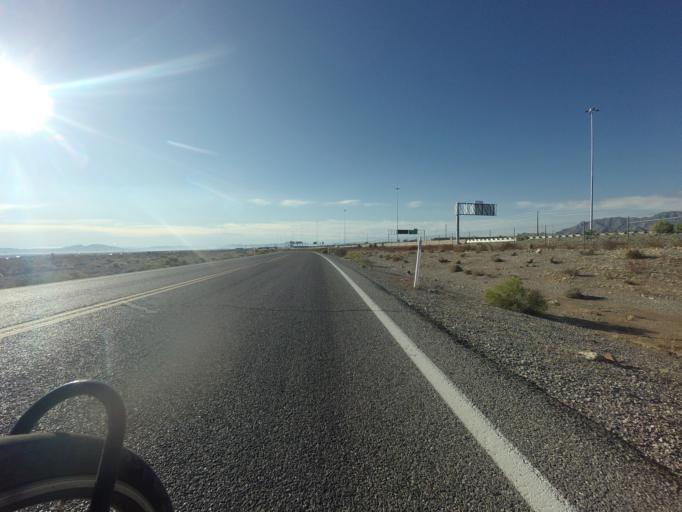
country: US
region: Nevada
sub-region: Clark County
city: Summerlin South
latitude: 36.3232
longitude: -115.3074
